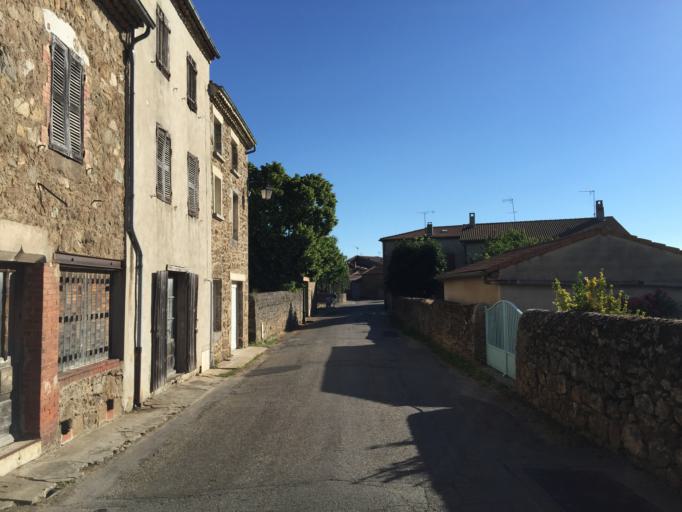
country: FR
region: Rhone-Alpes
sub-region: Departement de l'Ardeche
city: Satillieu
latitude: 45.1420
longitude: 4.6634
